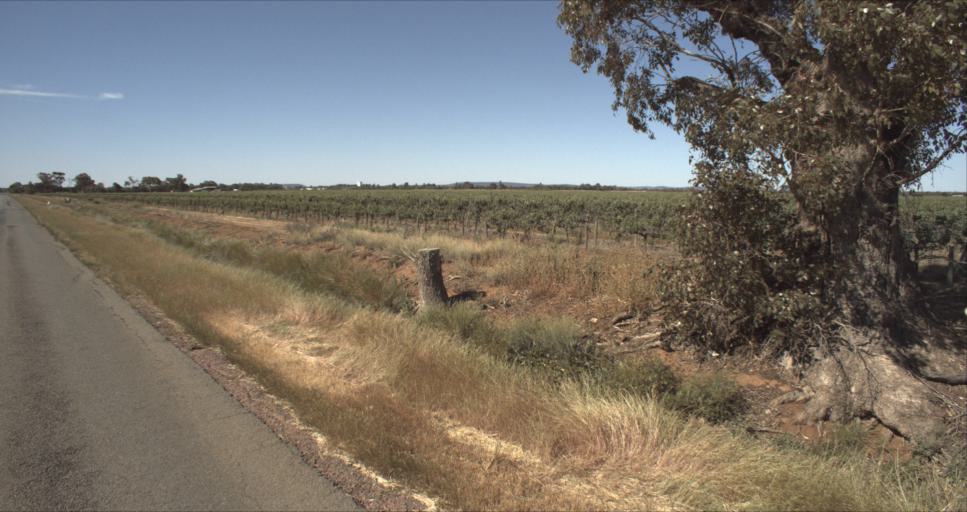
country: AU
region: New South Wales
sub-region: Leeton
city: Leeton
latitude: -34.5783
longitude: 146.3803
